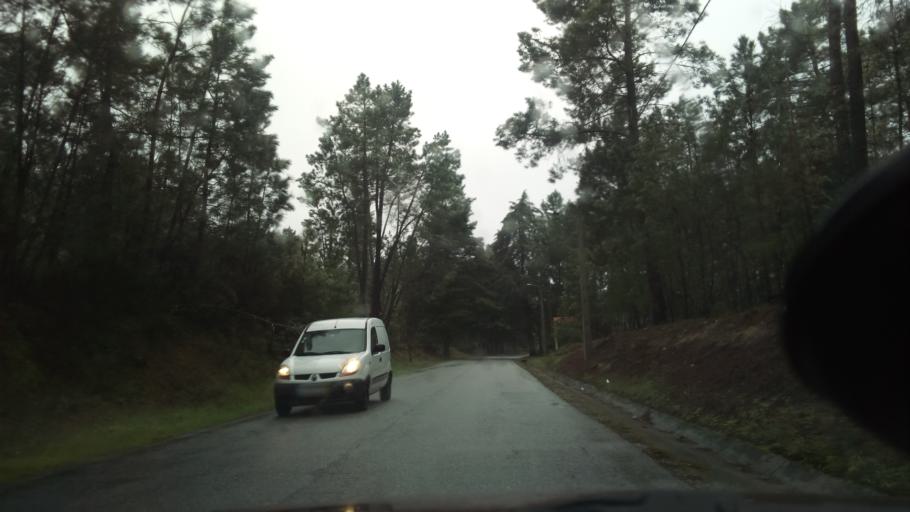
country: PT
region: Guarda
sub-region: Fornos de Algodres
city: Fornos de Algodres
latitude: 40.6099
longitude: -7.6260
